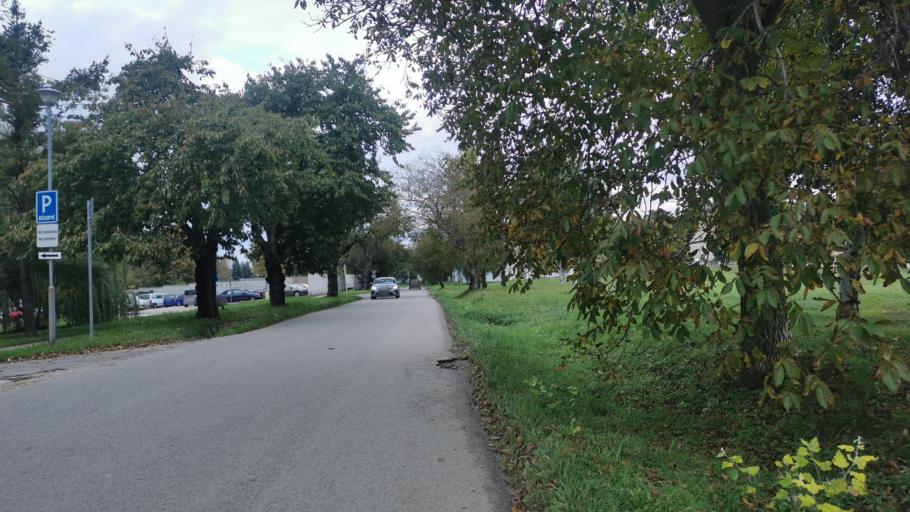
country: SK
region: Trnavsky
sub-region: Okres Skalica
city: Skalica
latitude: 48.8350
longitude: 17.2296
